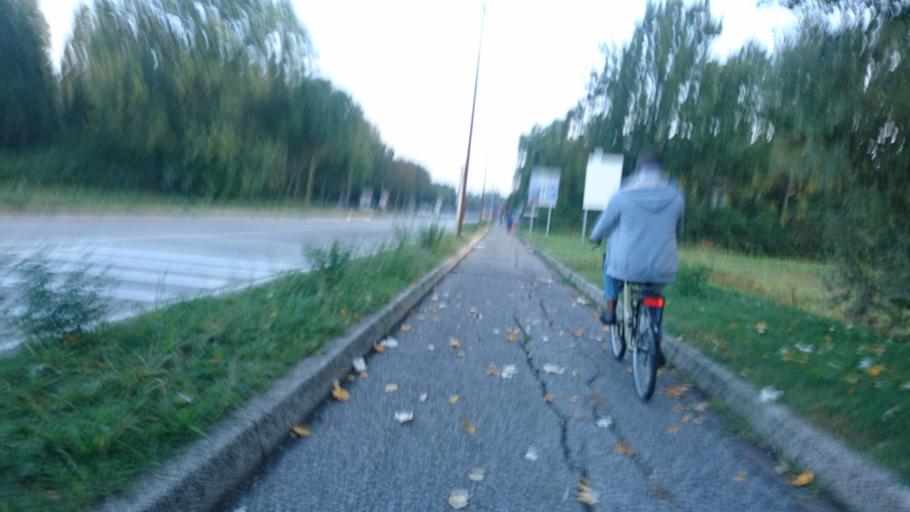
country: IT
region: Emilia-Romagna
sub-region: Provincia di Ferrara
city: Ferrara
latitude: 44.8551
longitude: 11.6144
